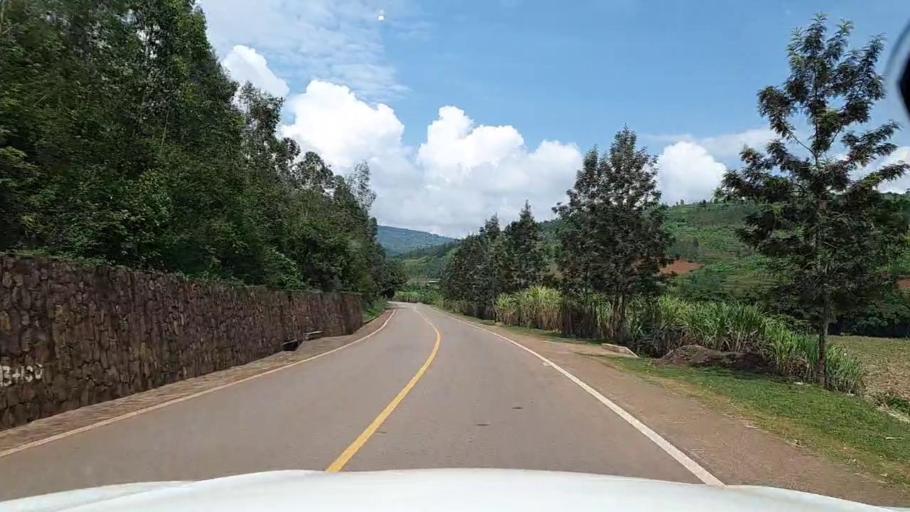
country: RW
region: Kigali
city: Kigali
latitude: -1.8449
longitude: 30.0942
